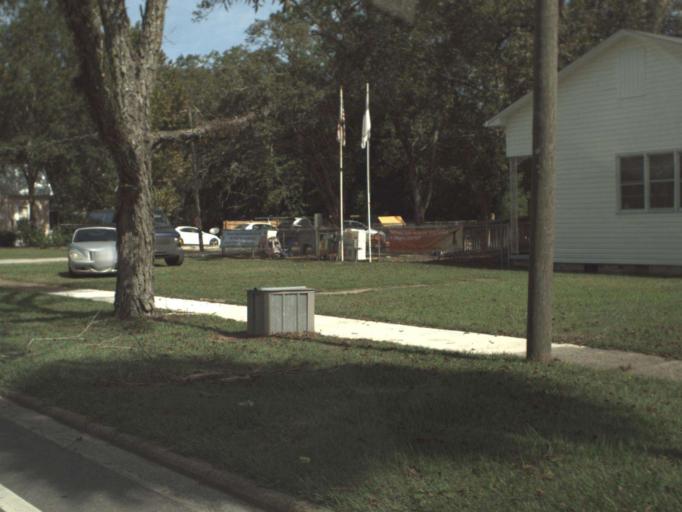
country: US
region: Florida
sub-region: Washington County
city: Chipley
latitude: 30.7761
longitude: -85.5380
